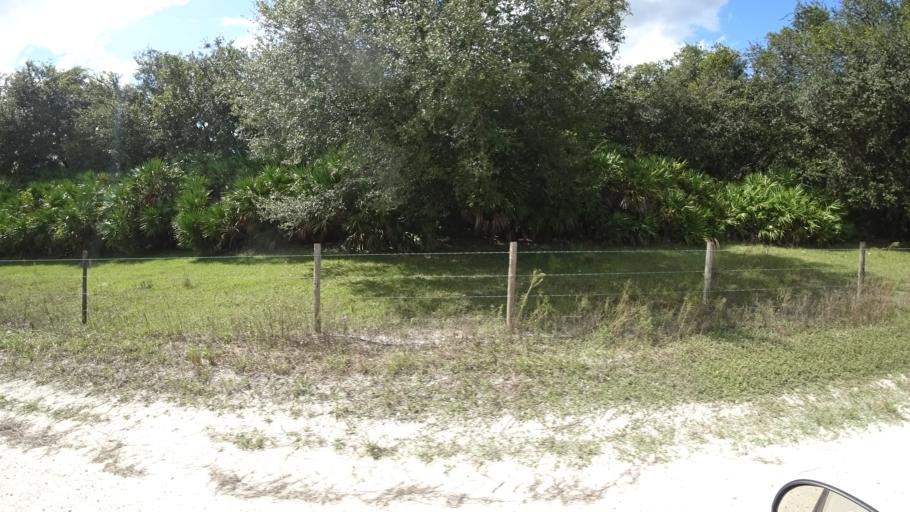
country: US
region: Florida
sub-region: DeSoto County
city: Arcadia
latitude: 27.3364
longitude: -82.1050
